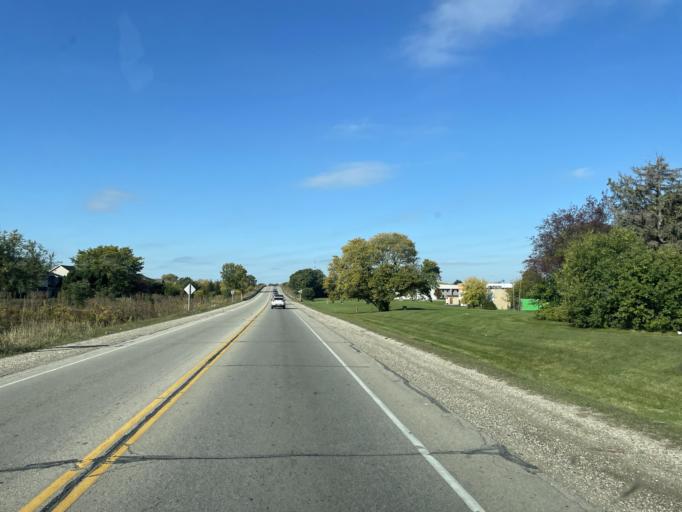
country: US
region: Wisconsin
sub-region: Kenosha County
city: Somers
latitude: 42.5890
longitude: -87.8916
